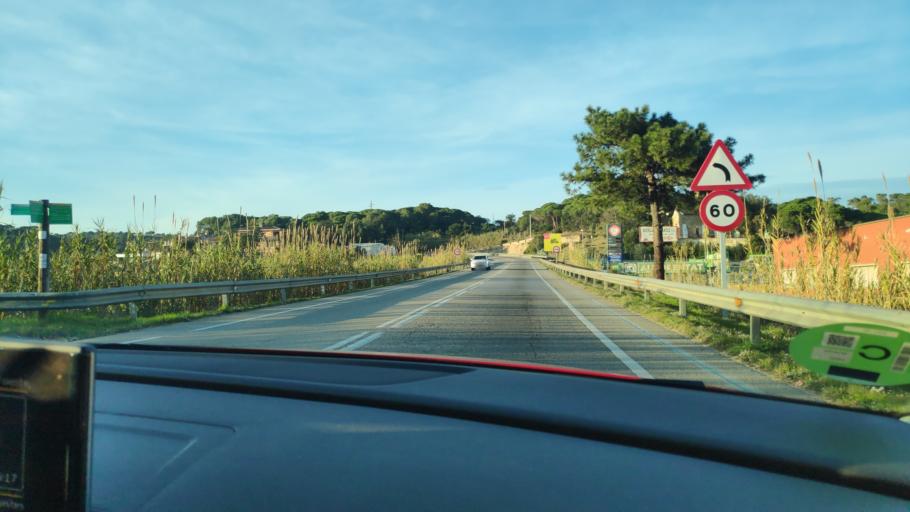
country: ES
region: Catalonia
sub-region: Provincia de Girona
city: Lloret de Mar
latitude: 41.7160
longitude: 2.8299
